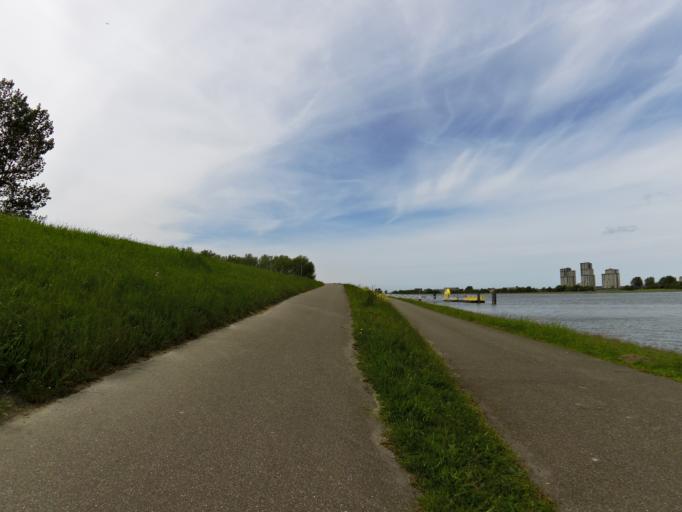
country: NL
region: South Holland
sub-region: Gemeente Maassluis
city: Maassluis
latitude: 51.9237
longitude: 4.2235
